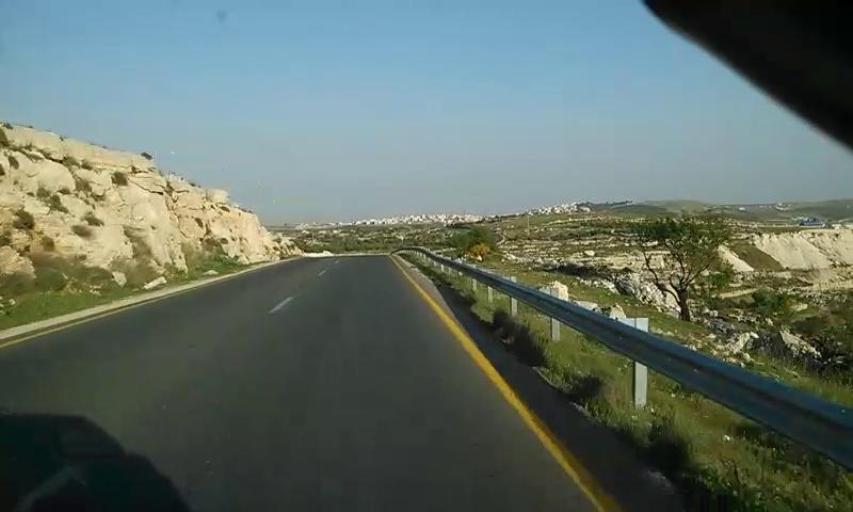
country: PS
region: West Bank
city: Marah Rabbah
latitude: 31.6477
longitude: 35.1841
